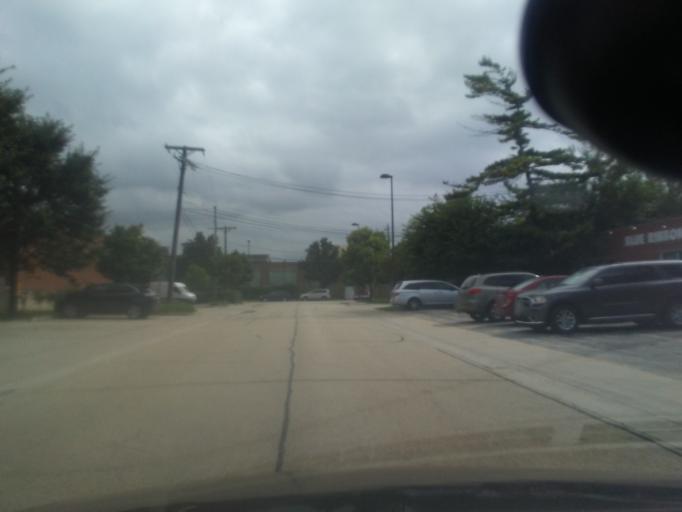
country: US
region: Illinois
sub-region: Cook County
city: Skokie
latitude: 42.0308
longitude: -87.7136
